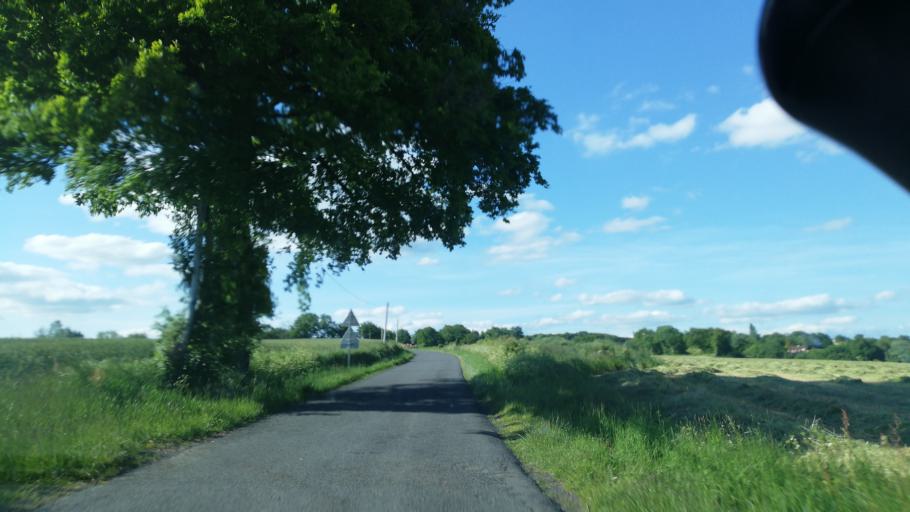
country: FR
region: Poitou-Charentes
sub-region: Departement des Deux-Sevres
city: Moncoutant
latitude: 46.7113
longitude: -0.5878
